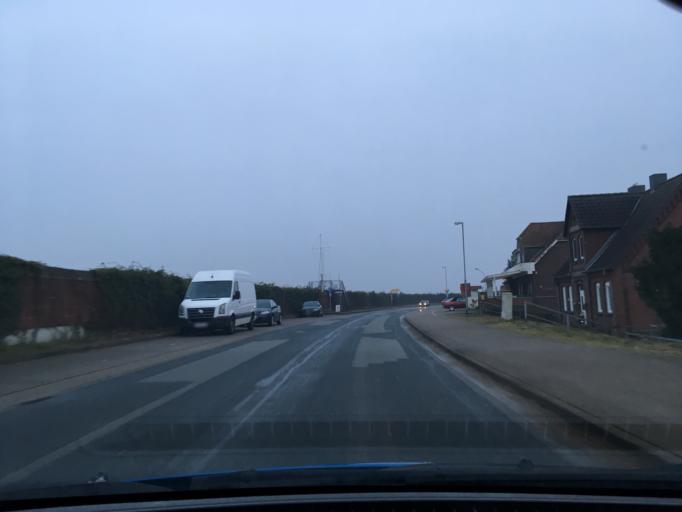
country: DE
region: Lower Saxony
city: Stelle
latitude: 53.4147
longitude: 10.1427
